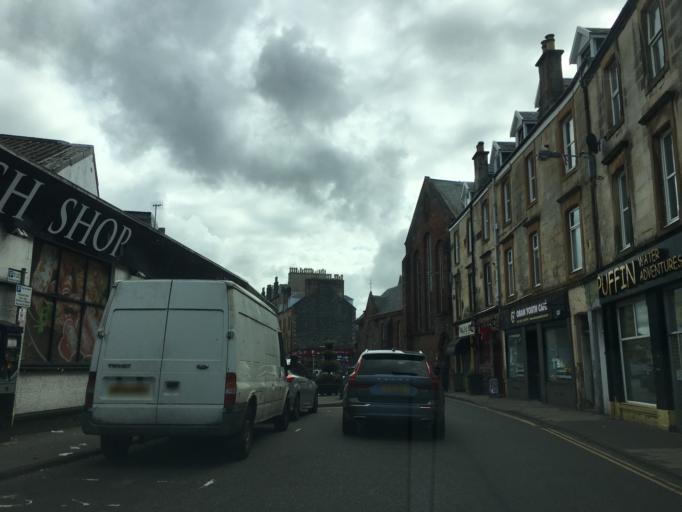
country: GB
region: Scotland
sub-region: Argyll and Bute
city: Oban
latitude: 56.4172
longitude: -5.4732
